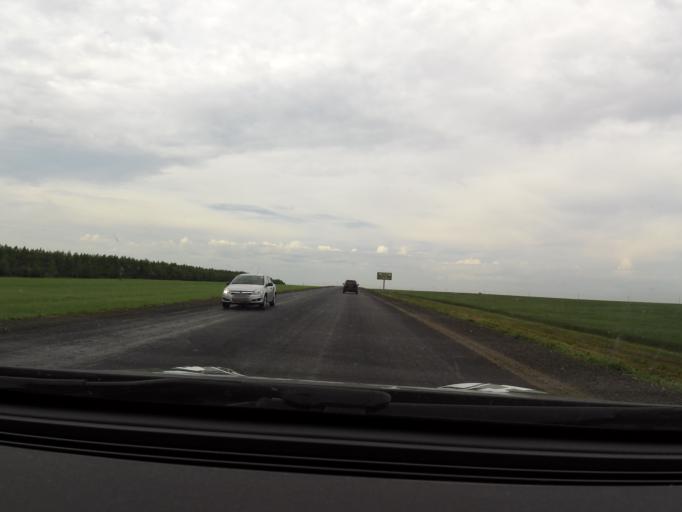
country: RU
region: Bashkortostan
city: Iglino
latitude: 54.7550
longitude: 56.3543
